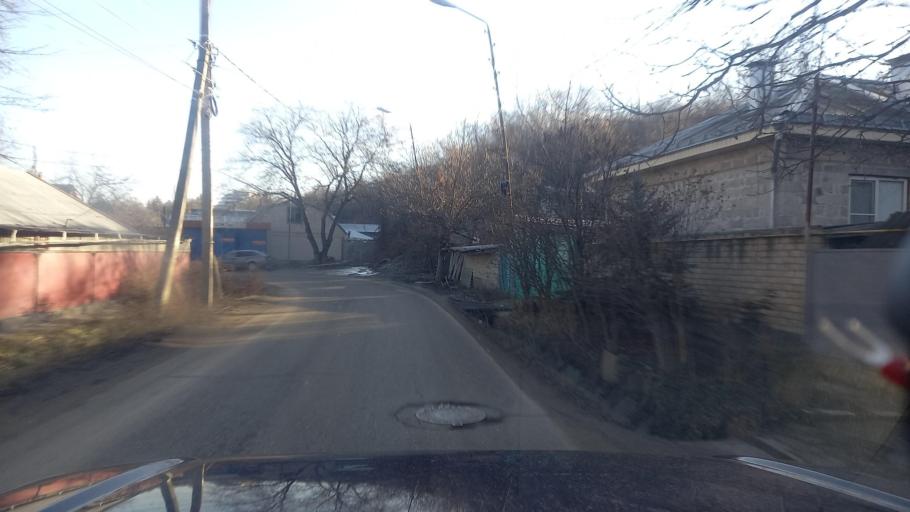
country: RU
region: Stavropol'skiy
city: Svobody
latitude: 44.0231
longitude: 43.0685
